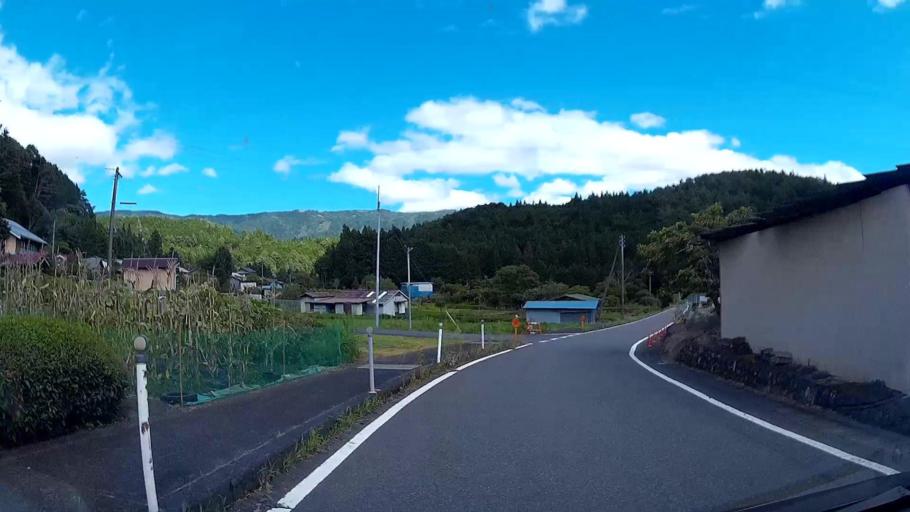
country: JP
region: Shizuoka
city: Shizuoka-shi
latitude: 35.2187
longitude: 138.2274
